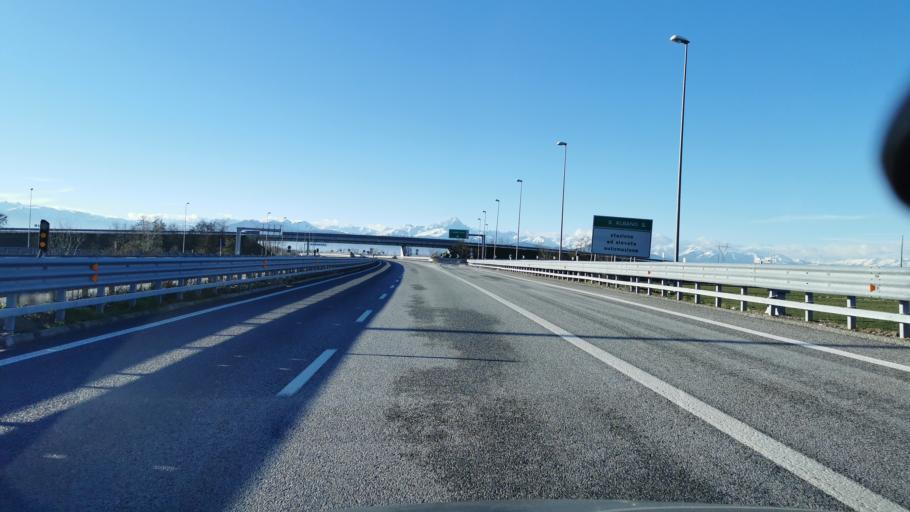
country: IT
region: Piedmont
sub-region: Provincia di Cuneo
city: Montanera
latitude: 44.4760
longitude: 7.6935
